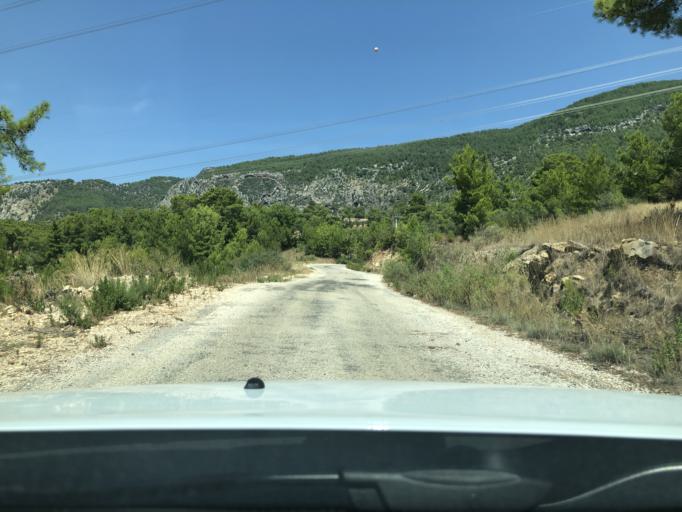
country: TR
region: Antalya
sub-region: Manavgat
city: Manavgat
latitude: 36.8770
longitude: 31.5503
